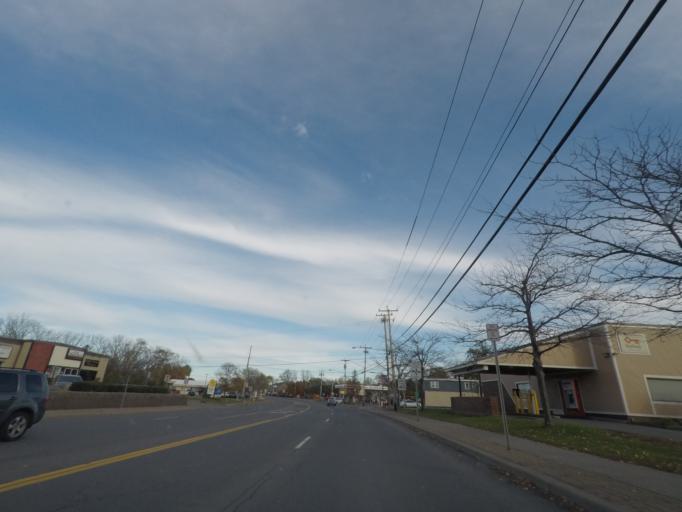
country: US
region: New York
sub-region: Albany County
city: Delmar
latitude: 42.6289
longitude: -73.8110
